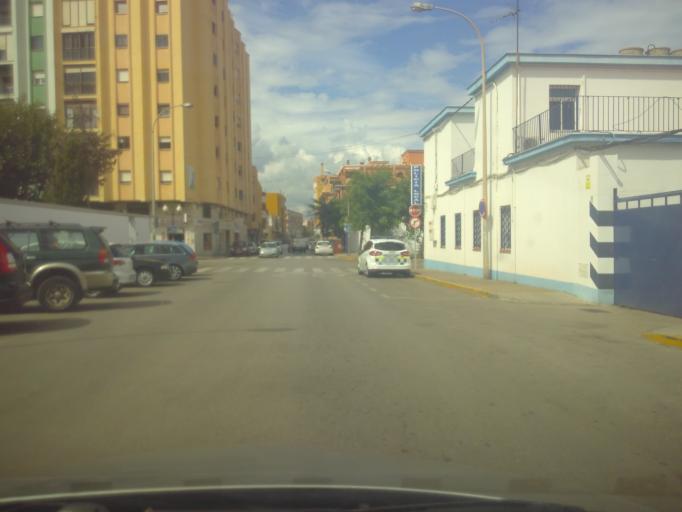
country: ES
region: Andalusia
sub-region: Provincia de Cadiz
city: La Linea de la Concepcion
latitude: 36.1609
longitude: -5.3473
